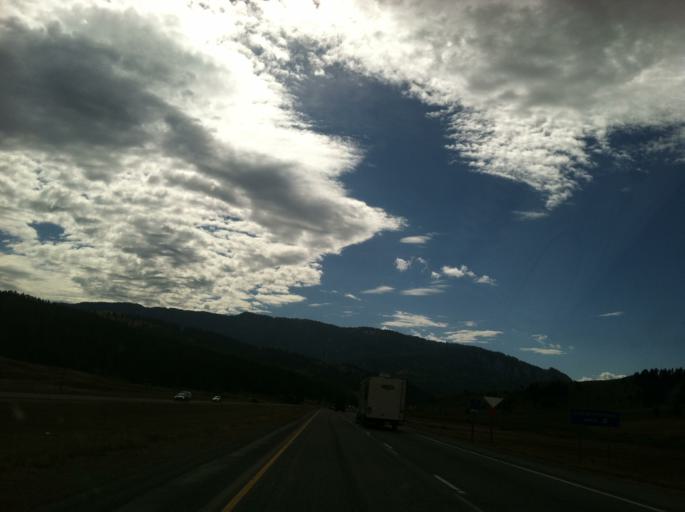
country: US
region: Montana
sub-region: Gallatin County
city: Bozeman
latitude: 45.6587
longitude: -110.8461
